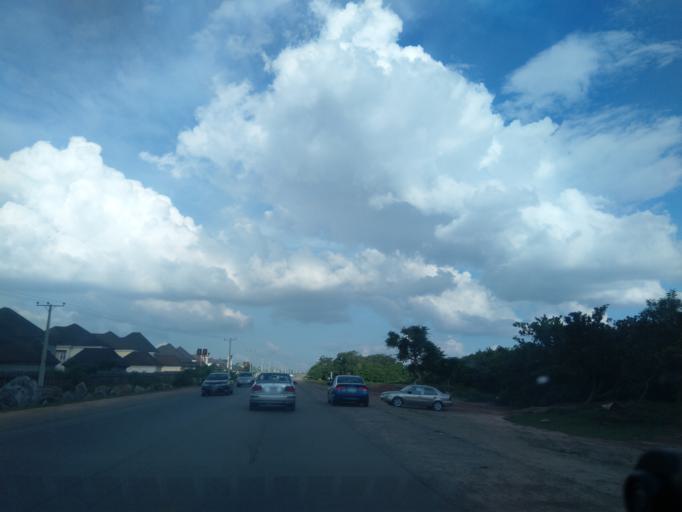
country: NG
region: Abuja Federal Capital Territory
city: Abuja
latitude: 9.0424
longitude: 7.3914
